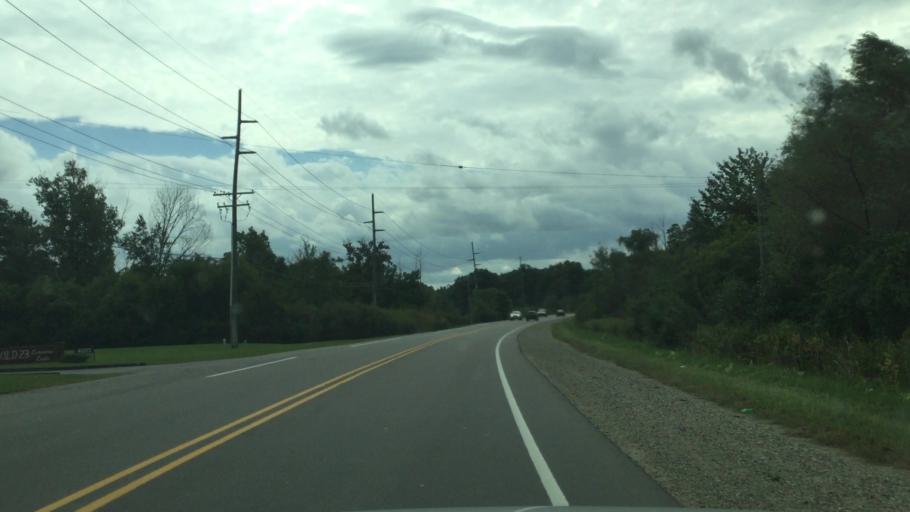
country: US
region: Michigan
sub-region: Livingston County
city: Brighton
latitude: 42.5452
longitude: -83.7512
